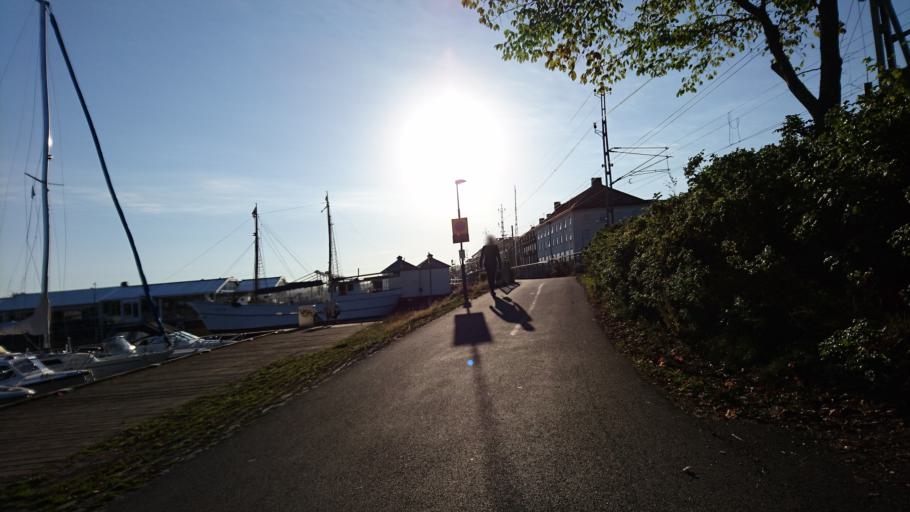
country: SE
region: Joenkoeping
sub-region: Jonkopings Kommun
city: Jonkoping
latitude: 57.7842
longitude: 14.1678
